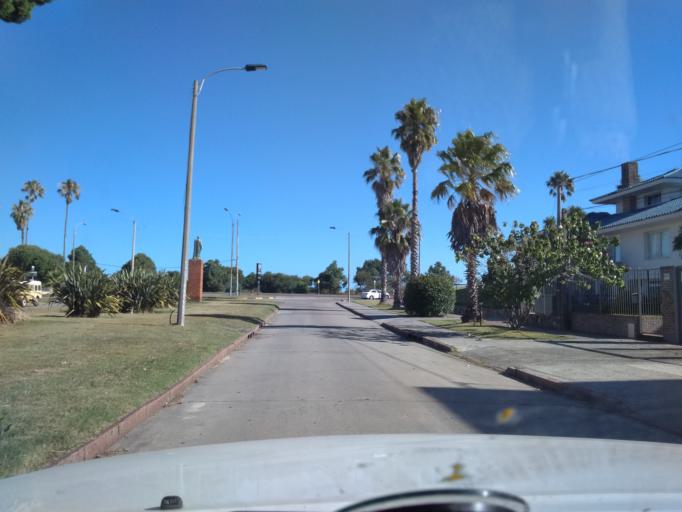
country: UY
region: Canelones
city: Paso de Carrasco
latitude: -34.8962
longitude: -56.0732
